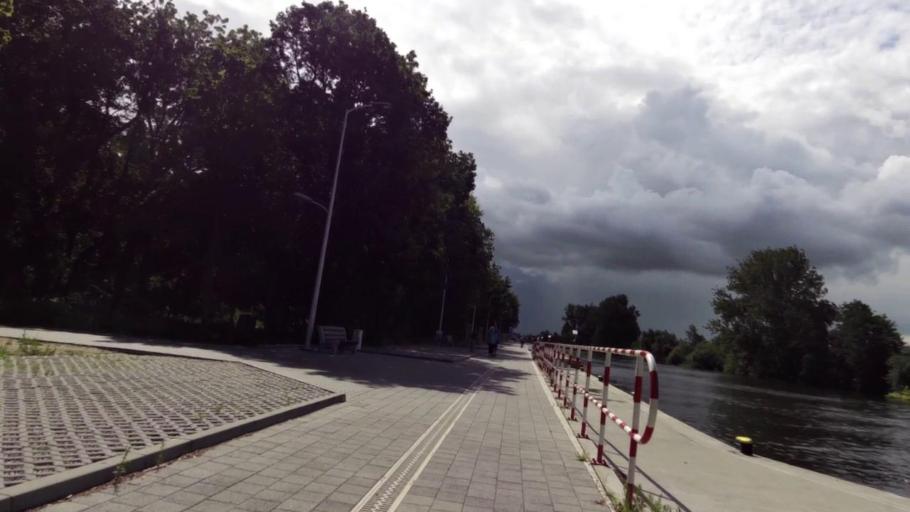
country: PL
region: West Pomeranian Voivodeship
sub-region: Powiat slawienski
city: Darlowo
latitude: 54.4317
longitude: 16.3919
